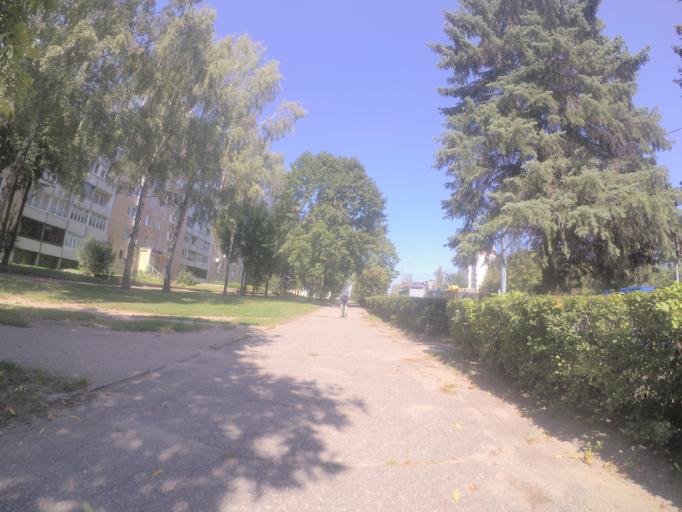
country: BY
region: Grodnenskaya
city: Hrodna
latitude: 53.6668
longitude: 23.8009
